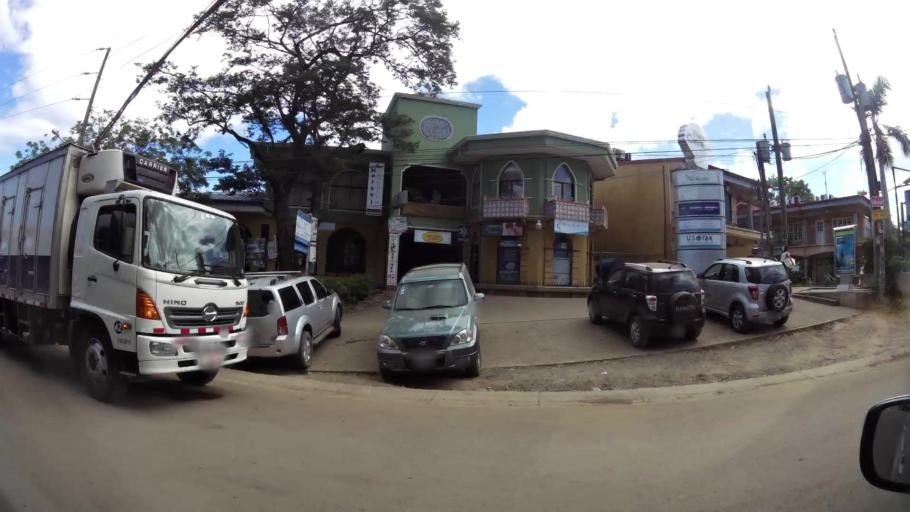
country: CR
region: Guanacaste
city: Santa Cruz
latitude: 10.2991
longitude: -85.8413
